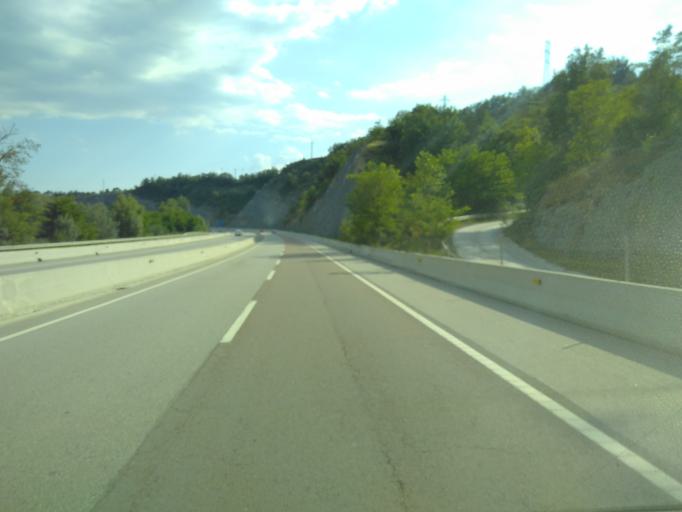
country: ES
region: Catalonia
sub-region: Provincia de Barcelona
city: Vilaseca
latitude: 42.0686
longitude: 2.2380
